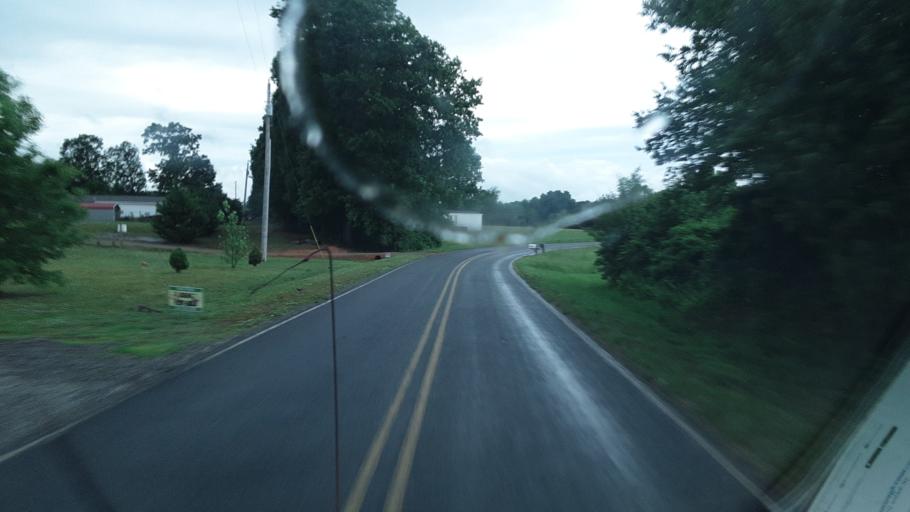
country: US
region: North Carolina
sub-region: Yadkin County
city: Jonesville
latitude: 36.0975
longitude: -80.8710
